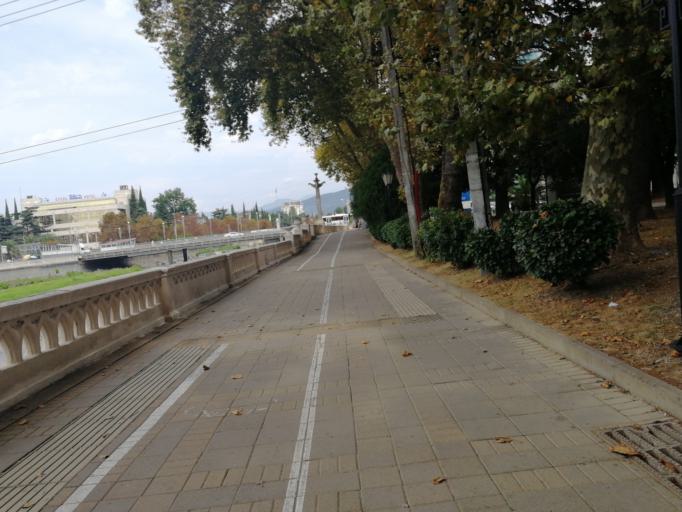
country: RU
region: Krasnodarskiy
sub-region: Sochi City
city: Sochi
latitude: 43.5933
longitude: 39.7209
